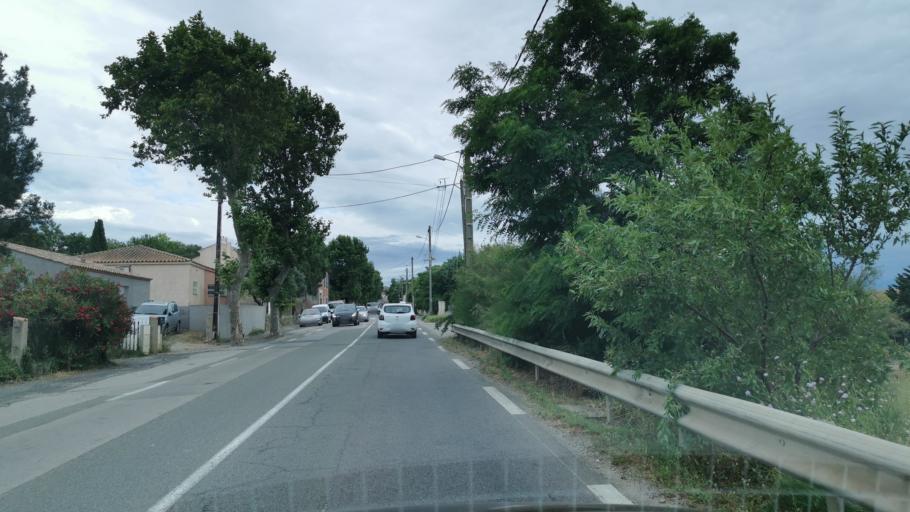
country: FR
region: Languedoc-Roussillon
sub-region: Departement de l'Aude
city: Marcorignan
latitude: 43.2301
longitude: 2.9237
